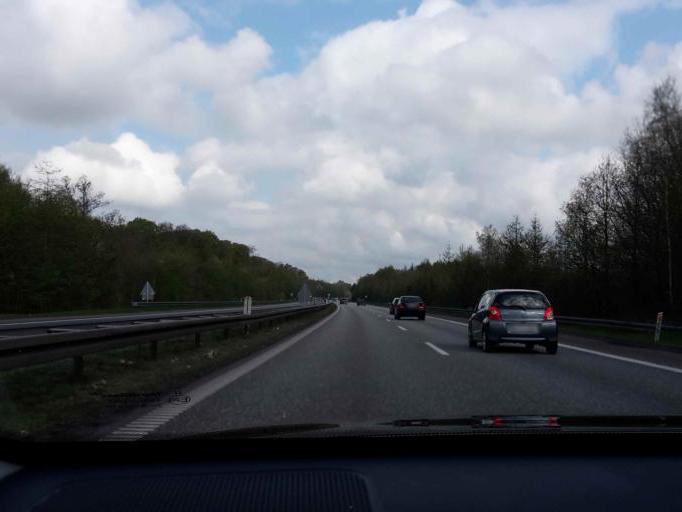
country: DK
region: South Denmark
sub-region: Fredericia Kommune
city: Taulov
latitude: 55.5571
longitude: 9.6304
